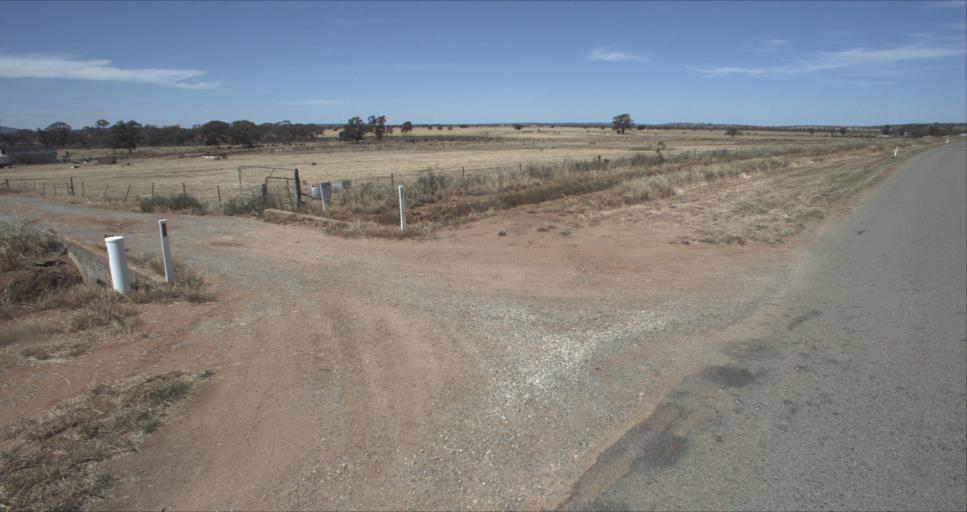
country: AU
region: New South Wales
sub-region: Leeton
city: Leeton
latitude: -34.5977
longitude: 146.4781
